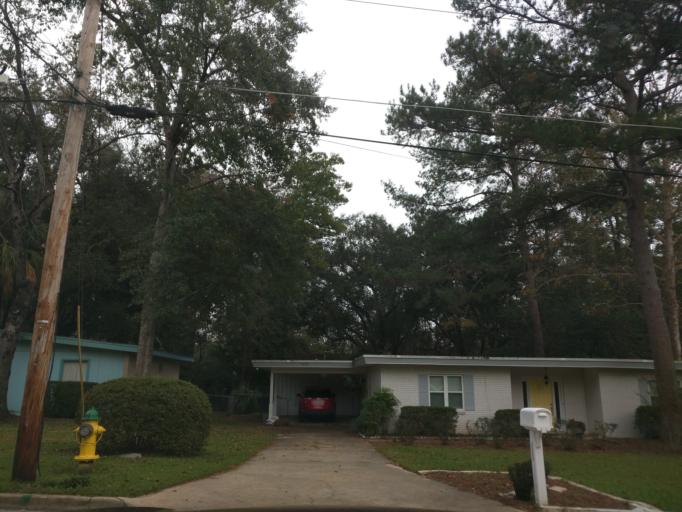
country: US
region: Florida
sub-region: Leon County
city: Tallahassee
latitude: 30.4570
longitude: -84.2506
